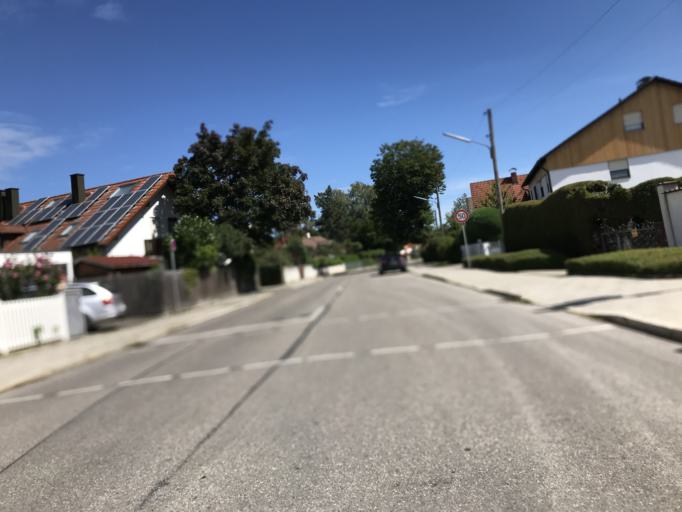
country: DE
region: Bavaria
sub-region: Upper Bavaria
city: Grobenzell
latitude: 48.1774
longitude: 11.3548
